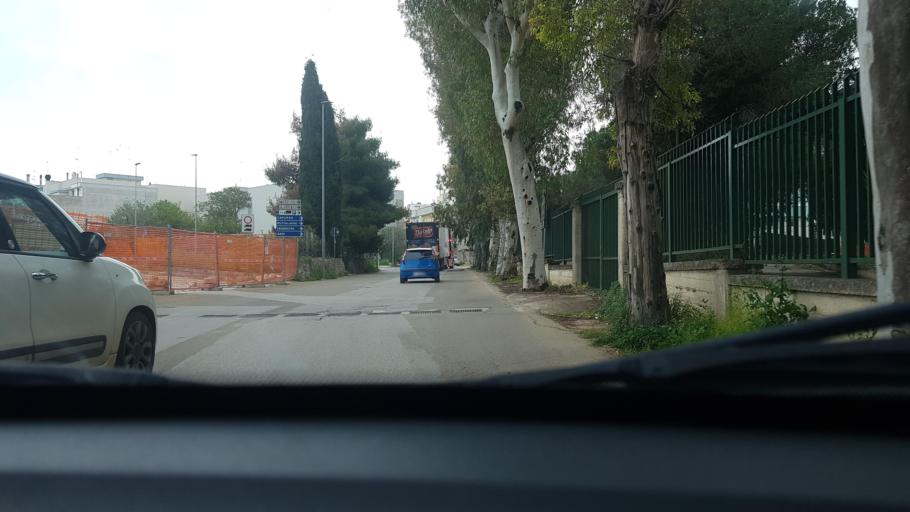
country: IT
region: Apulia
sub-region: Provincia di Bari
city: Noicattaro
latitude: 41.0365
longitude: 16.9828
